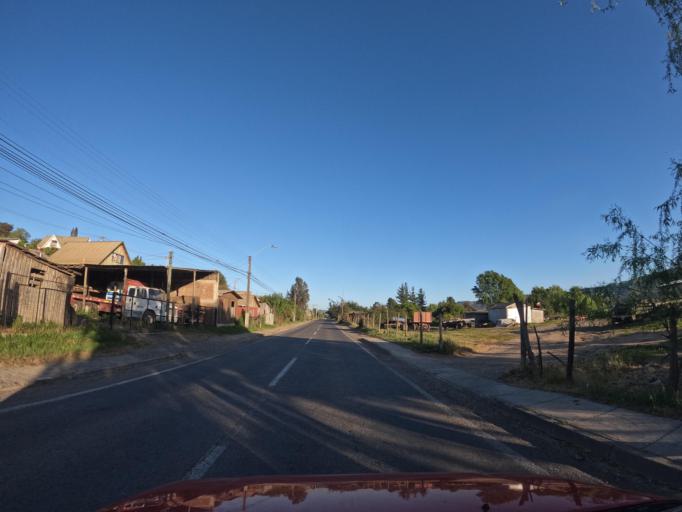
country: CL
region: Maule
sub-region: Provincia de Talca
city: Talca
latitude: -34.9917
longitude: -71.9791
